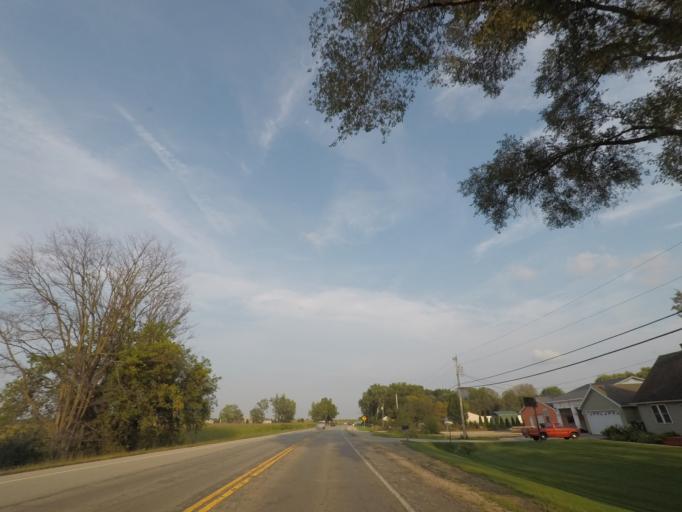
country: US
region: Wisconsin
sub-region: Dane County
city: Cottage Grove
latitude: 43.0896
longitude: -89.2388
